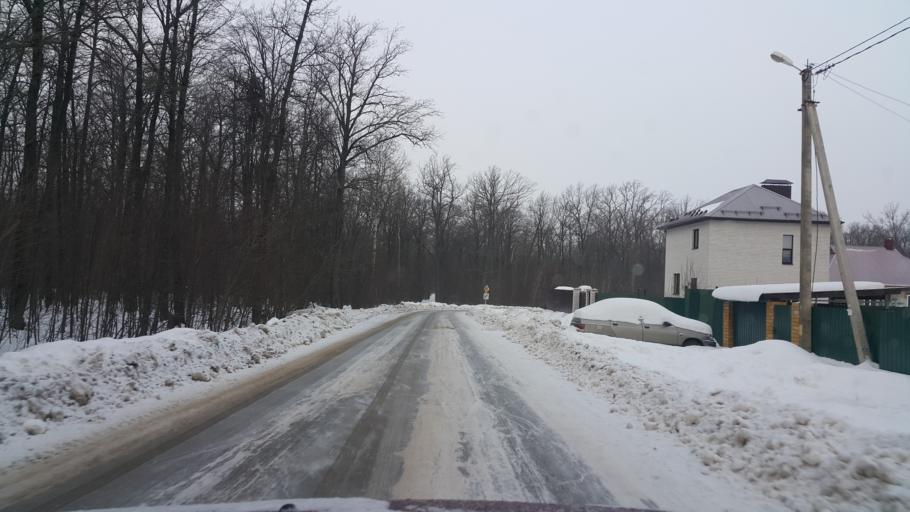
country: RU
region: Tambov
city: Kotovsk
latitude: 52.5717
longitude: 41.5231
